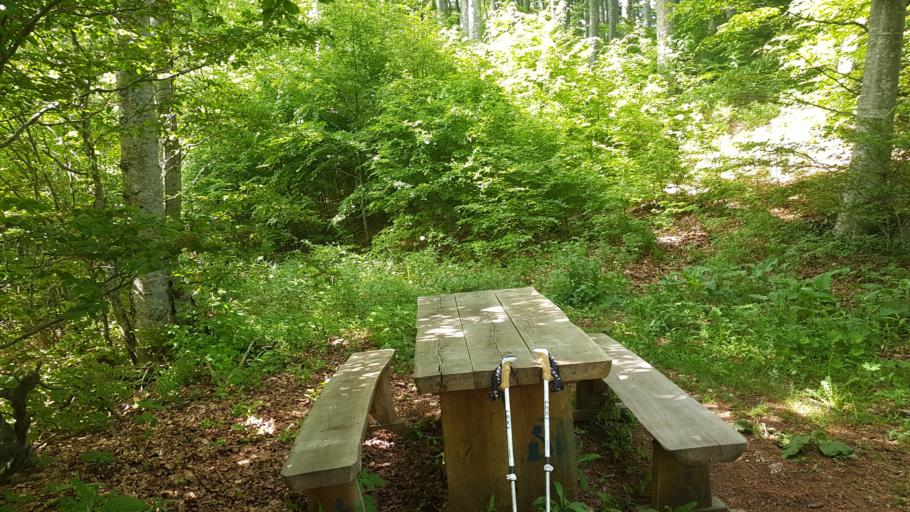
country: HR
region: Istarska
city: Lovran
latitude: 45.2828
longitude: 14.2093
